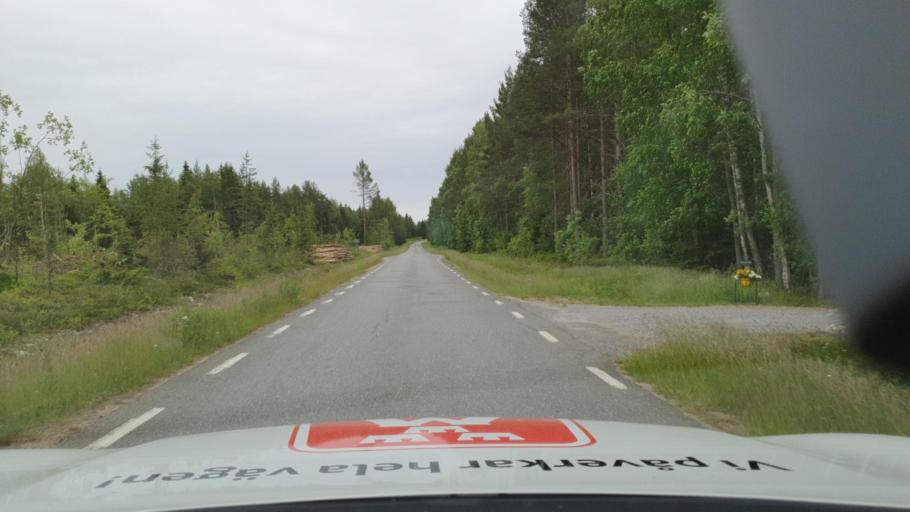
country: SE
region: Vaesterbotten
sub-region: Nordmalings Kommun
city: Nordmaling
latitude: 63.4744
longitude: 19.4607
